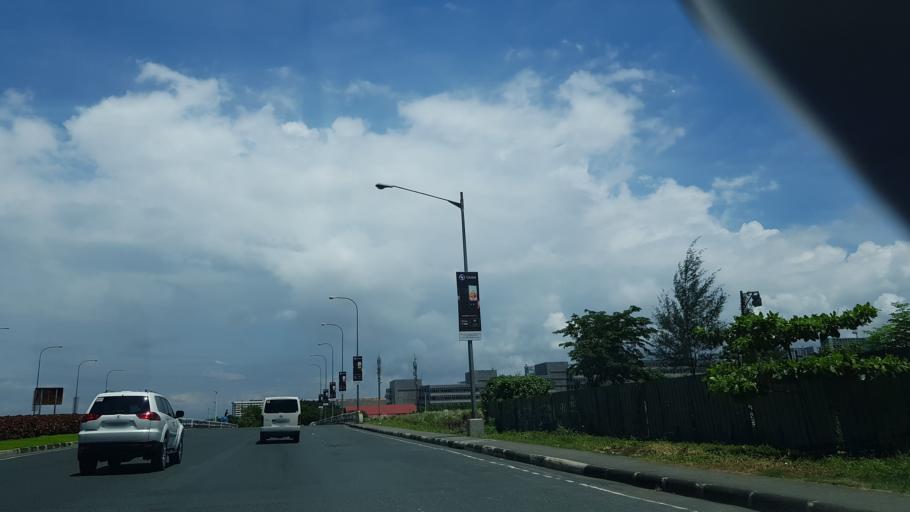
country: PH
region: Metro Manila
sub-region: City of Manila
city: Port Area
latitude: 14.5421
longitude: 120.9833
